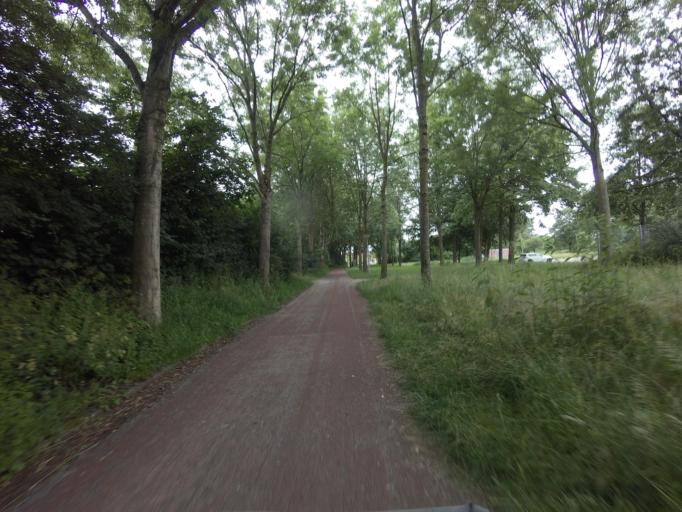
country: NL
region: North Holland
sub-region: Gemeente Huizen
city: Huizen
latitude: 52.2915
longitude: 5.2677
